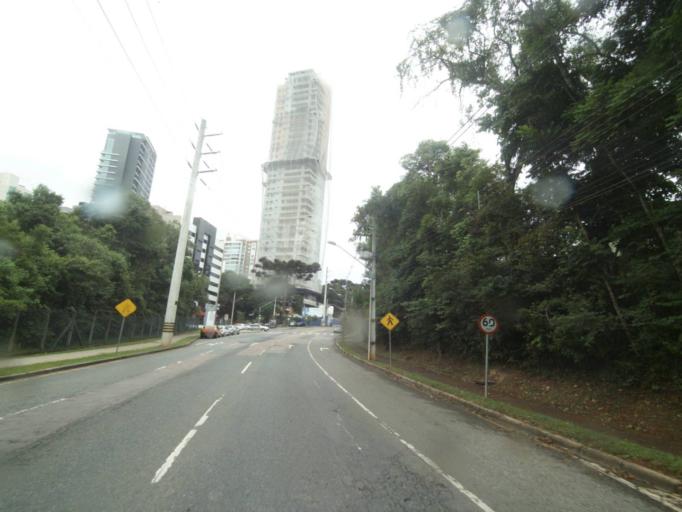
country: BR
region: Parana
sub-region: Curitiba
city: Curitiba
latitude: -25.4419
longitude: -49.3407
